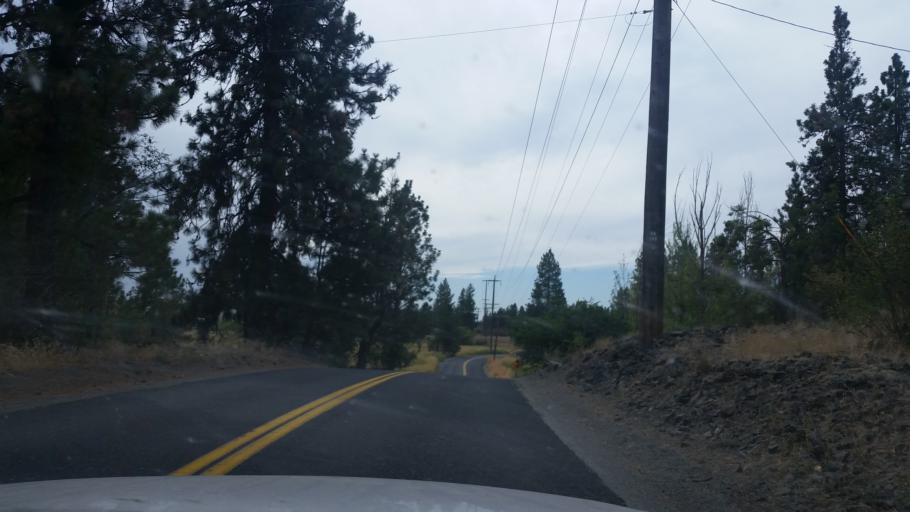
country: US
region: Washington
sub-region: Spokane County
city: Spokane
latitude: 47.6455
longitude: -117.4968
